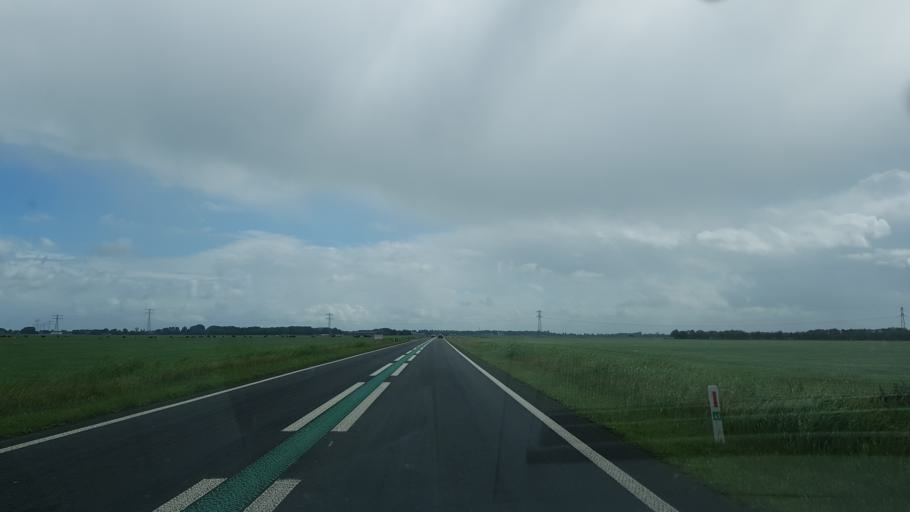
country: NL
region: Friesland
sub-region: Gemeente Dantumadiel
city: Rinsumageast
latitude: 53.3029
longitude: 5.9533
